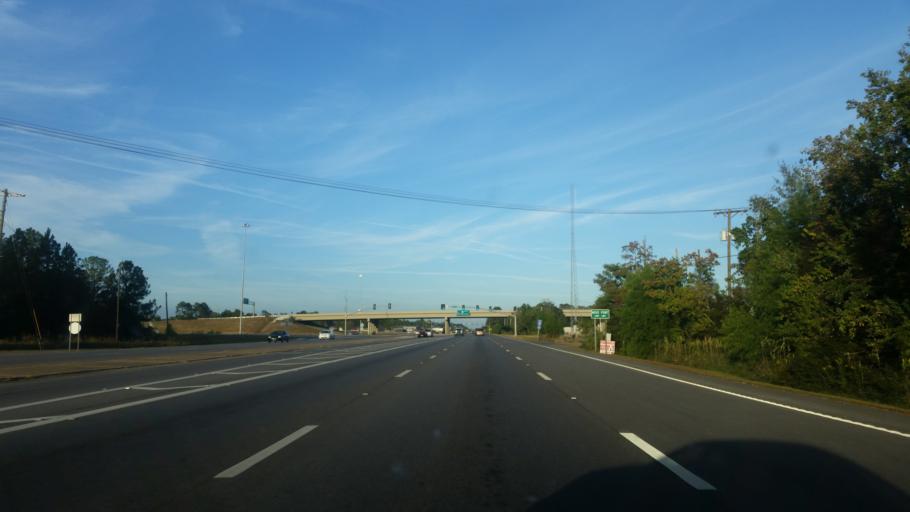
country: US
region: Mississippi
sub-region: Jackson County
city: Moss Point
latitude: 30.3891
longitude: -88.5093
